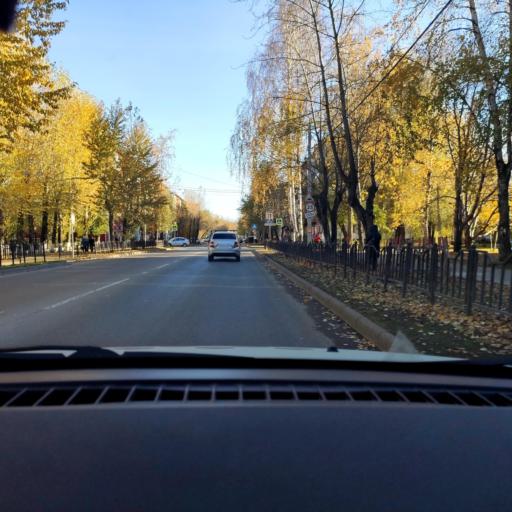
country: RU
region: Perm
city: Perm
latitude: 58.1057
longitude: 56.3831
